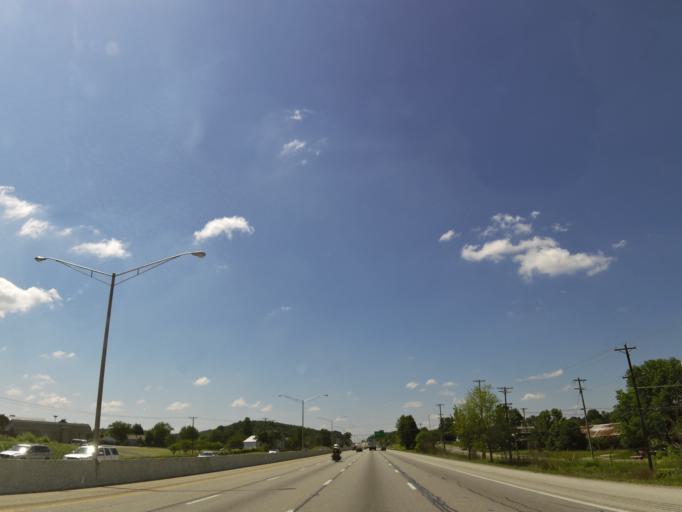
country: US
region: Kentucky
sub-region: Laurel County
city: London
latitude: 37.1320
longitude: -84.1086
